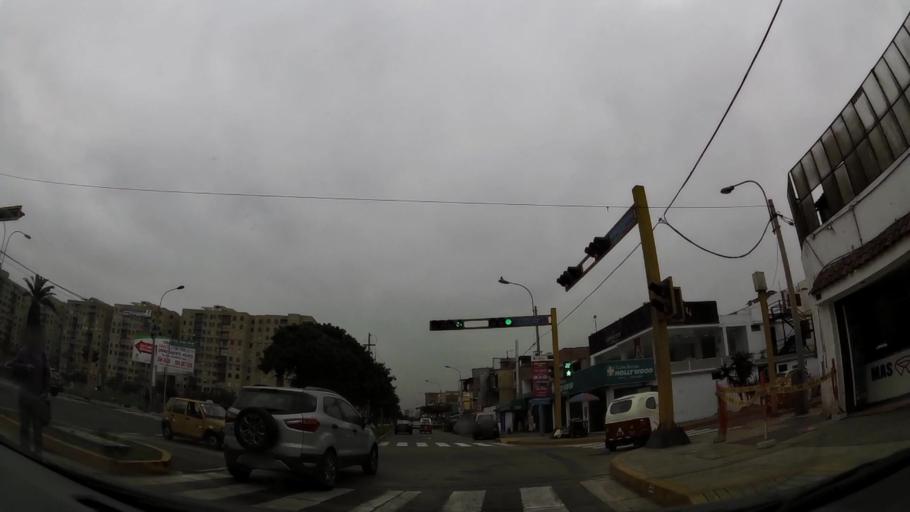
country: PE
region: Callao
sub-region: Callao
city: Callao
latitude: -12.0842
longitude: -77.0899
